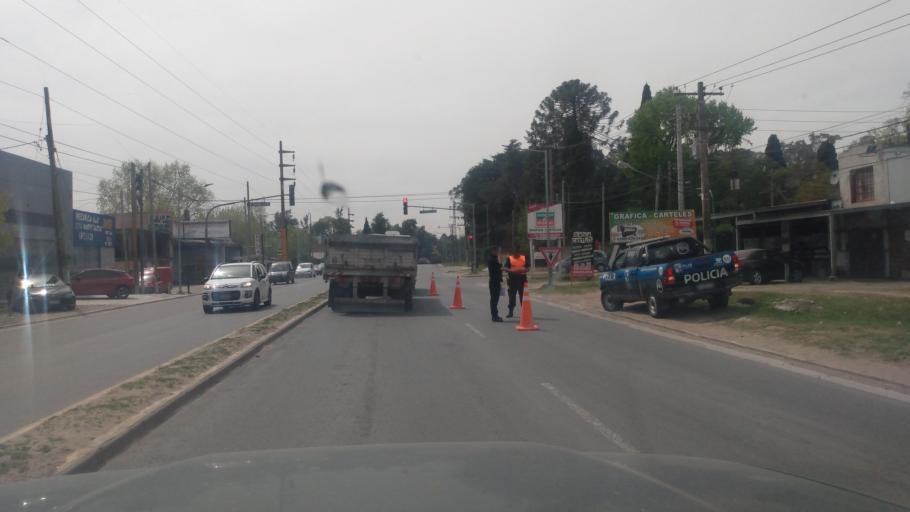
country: AR
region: Buenos Aires
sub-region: Partido de Pilar
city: Pilar
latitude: -34.4442
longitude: -58.9009
